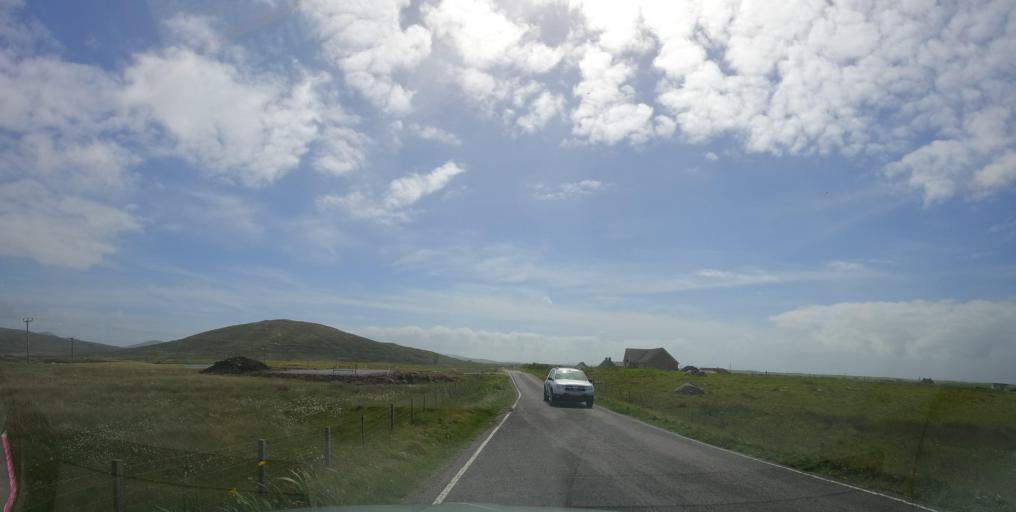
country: GB
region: Scotland
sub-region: Eilean Siar
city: Isle of South Uist
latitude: 57.1986
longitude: -7.3905
